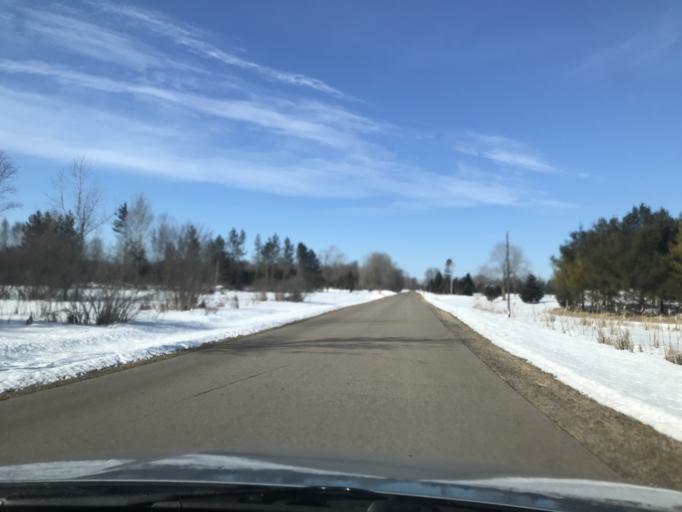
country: US
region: Wisconsin
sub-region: Oconto County
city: Oconto Falls
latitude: 44.9232
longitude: -88.1759
